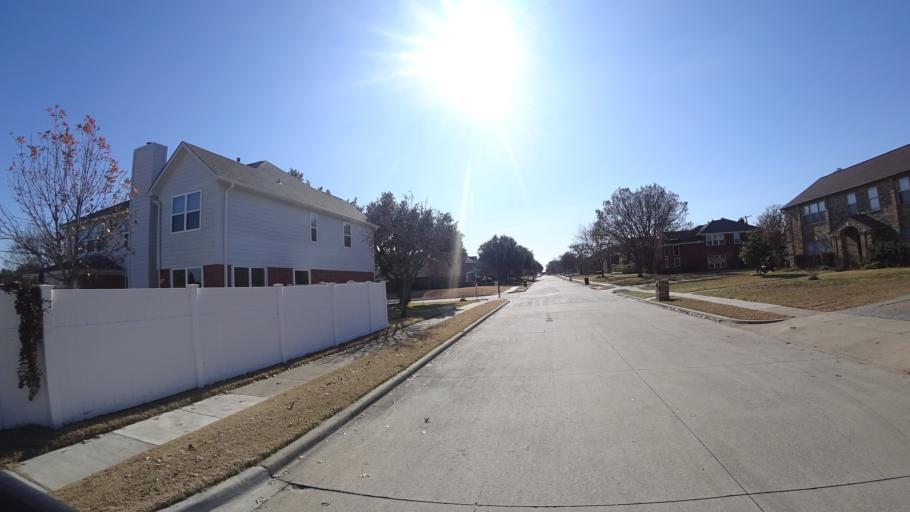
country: US
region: Texas
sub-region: Denton County
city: Lewisville
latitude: 33.0147
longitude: -97.0158
